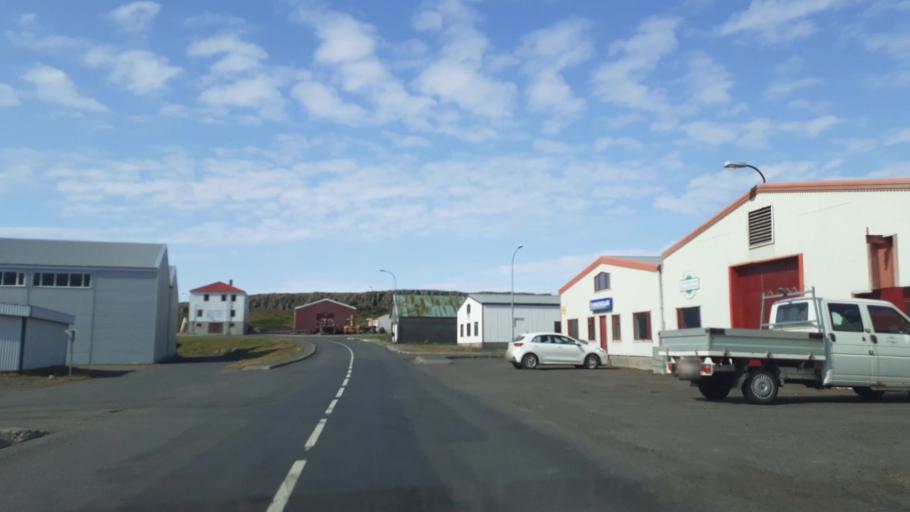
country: IS
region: Northwest
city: Saudarkrokur
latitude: 65.8271
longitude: -20.3155
